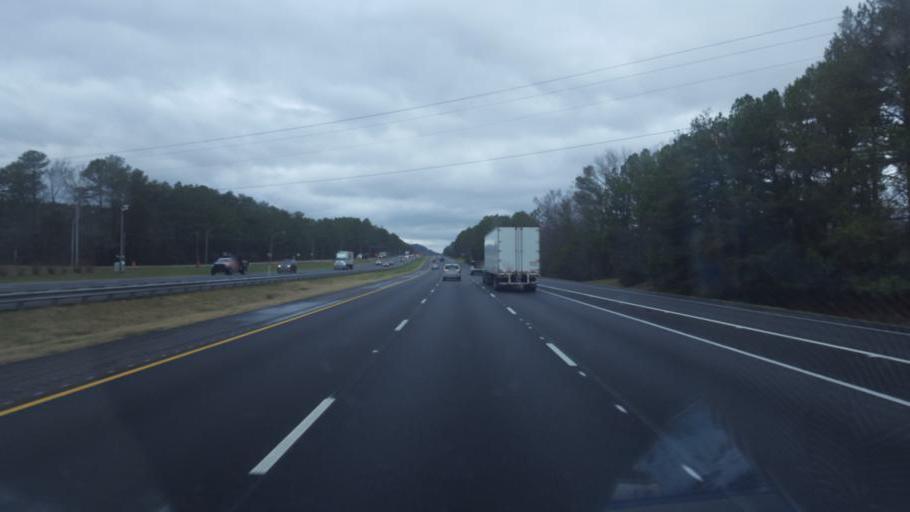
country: US
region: Georgia
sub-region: Catoosa County
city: Ringgold
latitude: 34.8812
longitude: -85.0520
